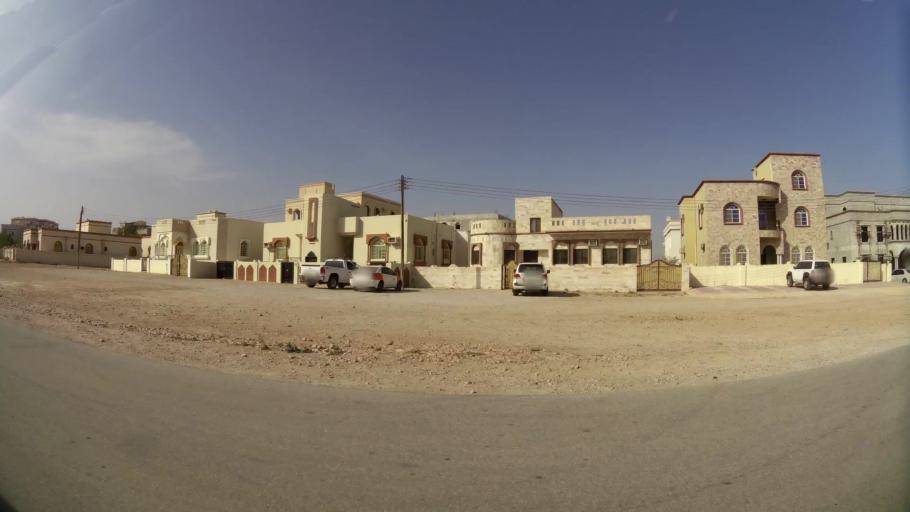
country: OM
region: Zufar
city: Salalah
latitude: 17.0070
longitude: 54.0159
